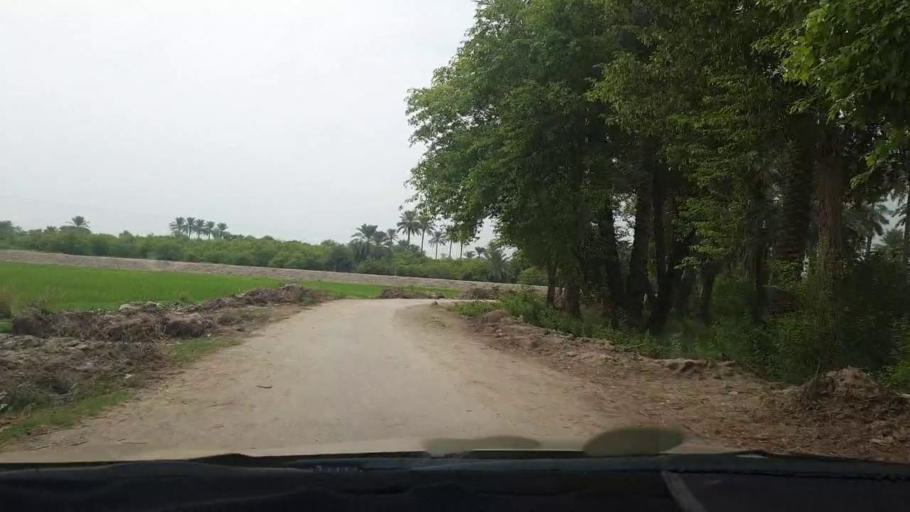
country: PK
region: Sindh
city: Larkana
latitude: 27.5722
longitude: 68.2443
